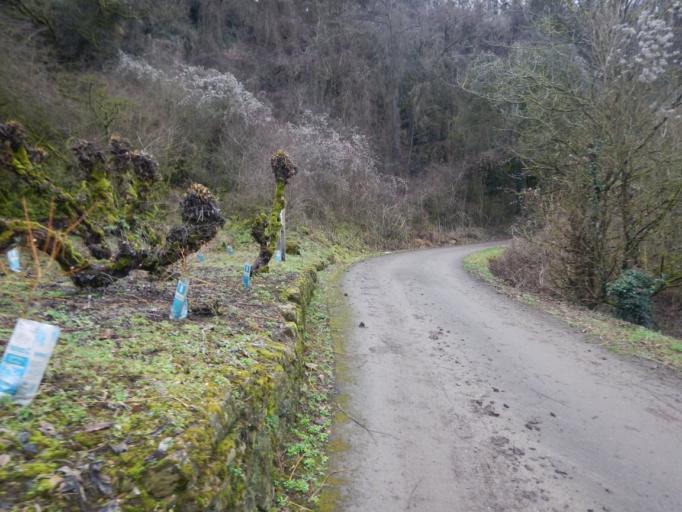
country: DE
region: Rheinland-Pfalz
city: Wellen
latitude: 49.6589
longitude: 6.4216
